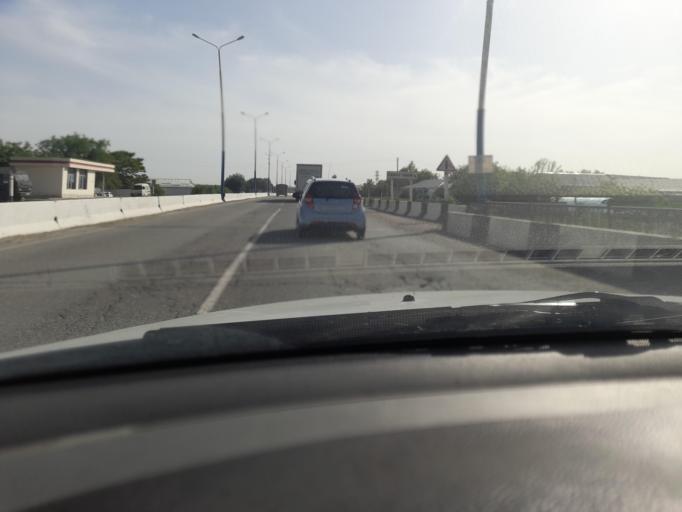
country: UZ
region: Samarqand
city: Kattaqo'rg'on
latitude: 39.9257
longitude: 66.3577
